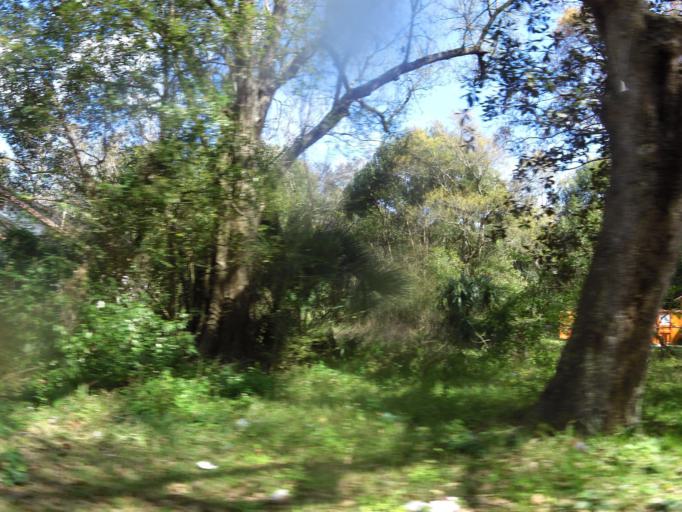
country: US
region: Florida
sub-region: Duval County
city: Jacksonville
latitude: 30.3311
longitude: -81.7182
